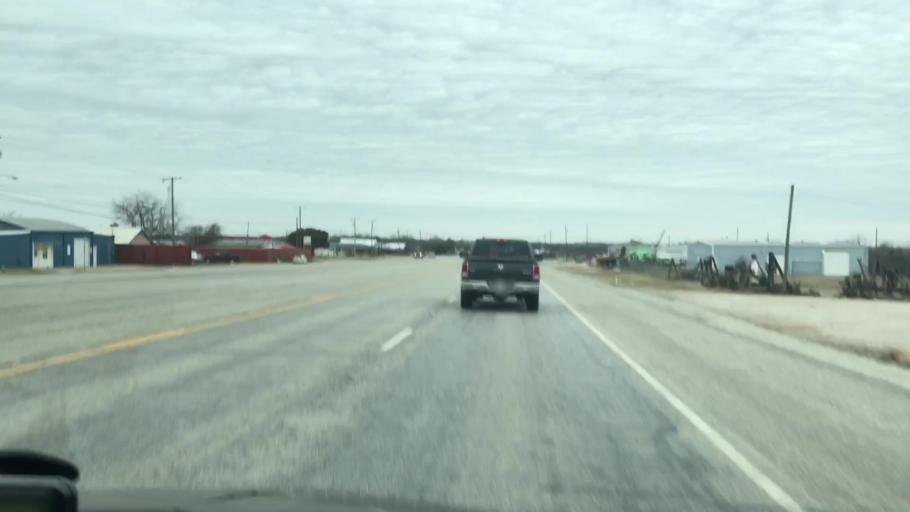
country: US
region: Texas
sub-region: Jack County
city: Jacksboro
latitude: 33.2018
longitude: -98.1503
